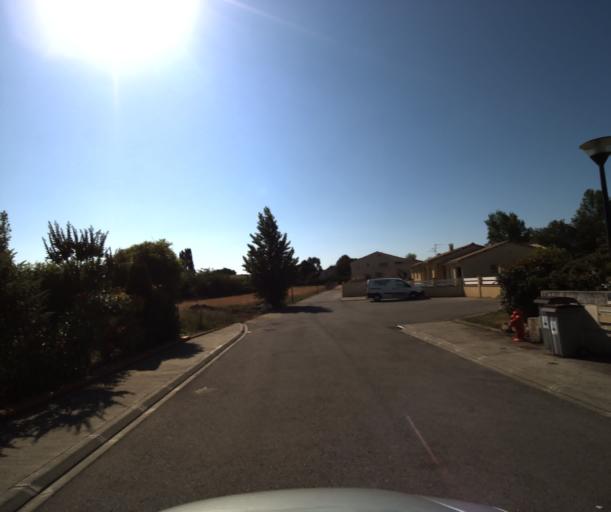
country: FR
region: Midi-Pyrenees
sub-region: Departement de la Haute-Garonne
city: Eaunes
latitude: 43.4284
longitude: 1.3564
